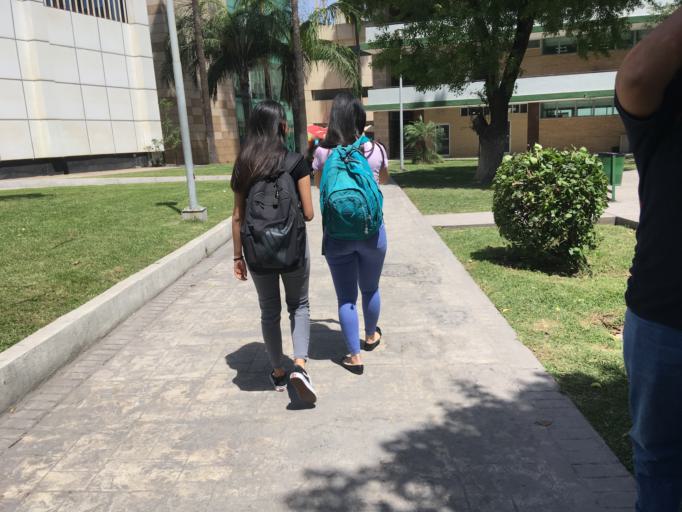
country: MX
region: Nuevo Leon
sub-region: San Nicolas de los Garza
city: San Nicolas de los Garza
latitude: 25.7258
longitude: -100.3109
